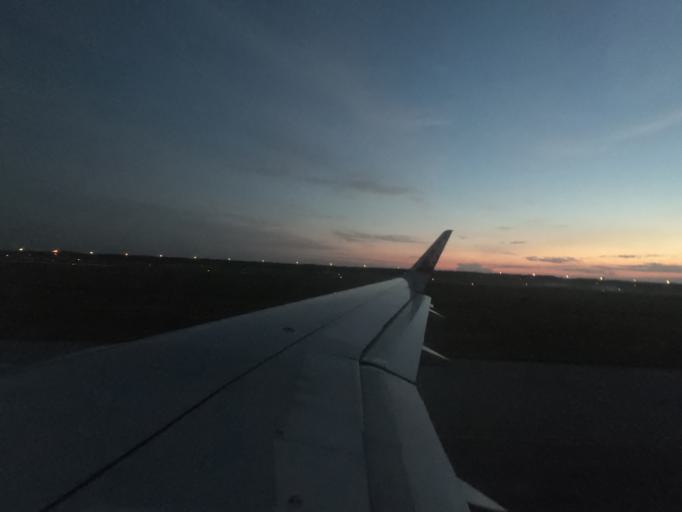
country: MY
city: Sungai Pelek New Village
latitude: 2.7139
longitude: 101.6958
